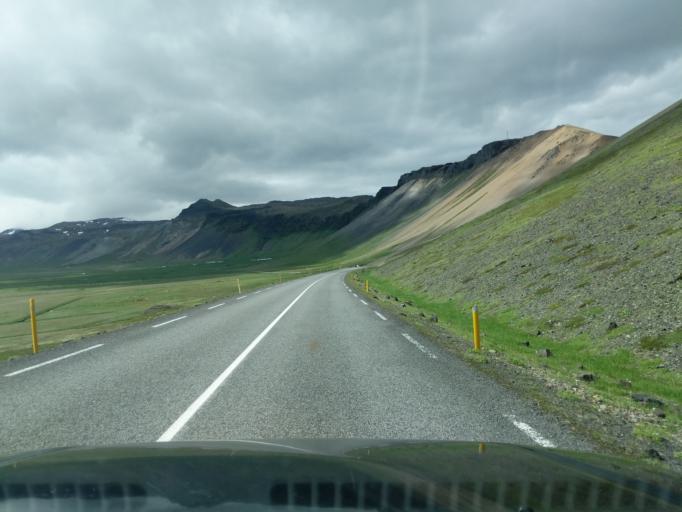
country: IS
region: West
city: Olafsvik
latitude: 64.8249
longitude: -23.4483
